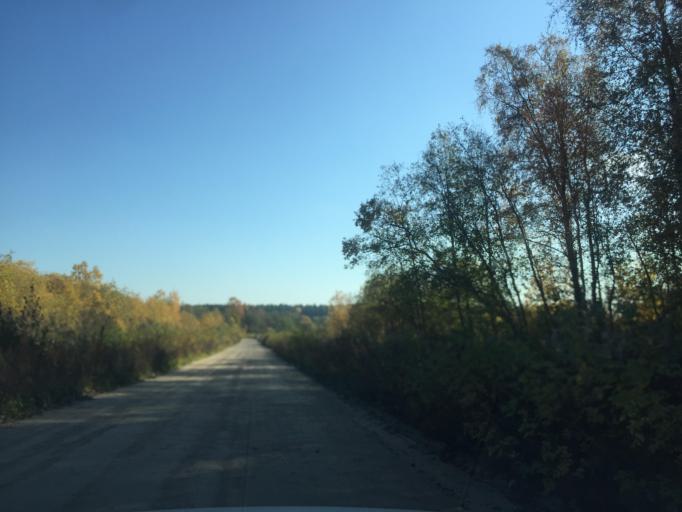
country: RU
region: Leningrad
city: Kuznechnoye
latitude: 61.2965
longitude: 30.0620
